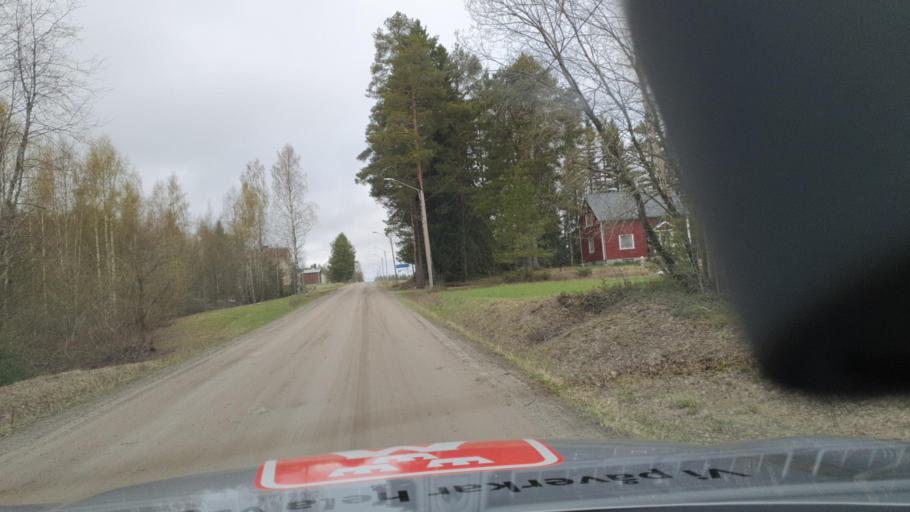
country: SE
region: Vaesterbotten
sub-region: Bjurholms Kommun
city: Bjurholm
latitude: 63.6476
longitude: 19.0518
